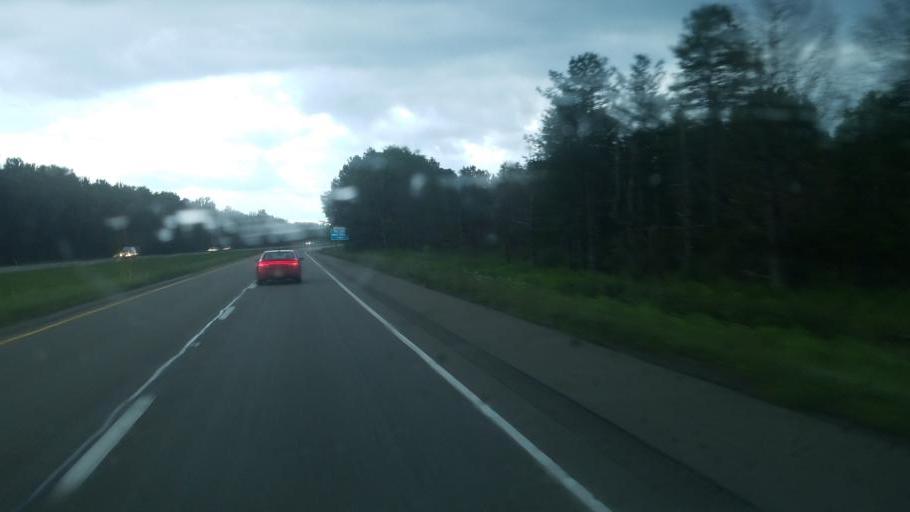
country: US
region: Pennsylvania
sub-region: Mercer County
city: Grove City
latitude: 41.1198
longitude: -80.1484
